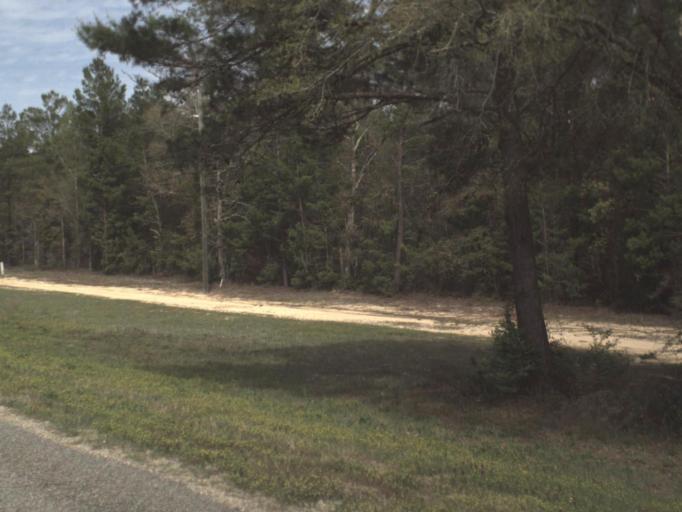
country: US
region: Florida
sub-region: Okaloosa County
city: Crestview
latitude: 30.7431
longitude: -86.3979
